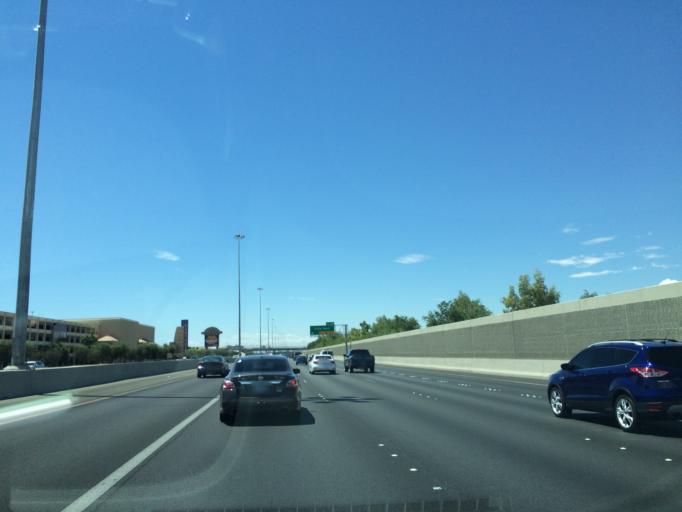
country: US
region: Nevada
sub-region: Clark County
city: Las Vegas
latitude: 36.2535
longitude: -115.2469
